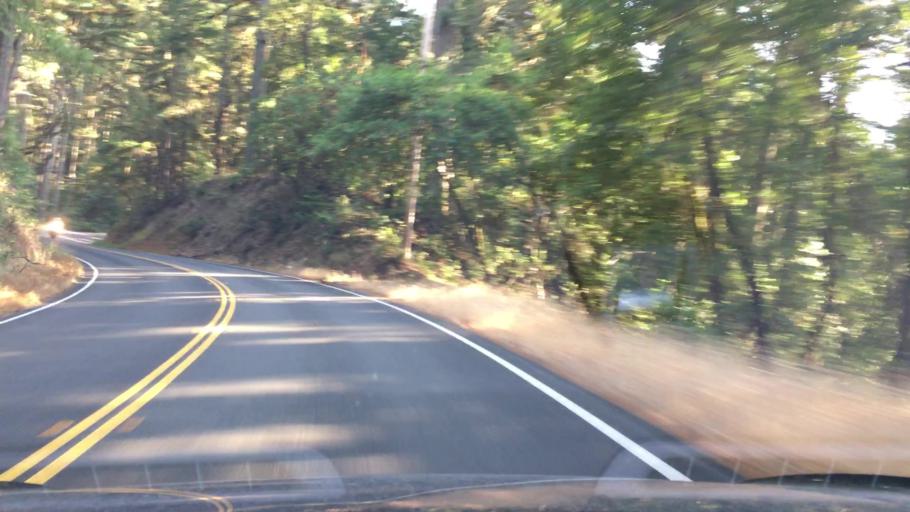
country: US
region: California
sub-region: Santa Clara County
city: Loyola
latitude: 37.2788
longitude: -122.1496
